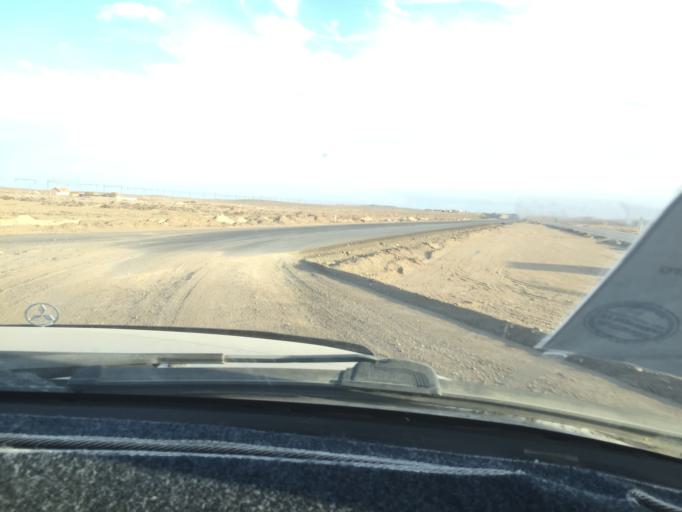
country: KZ
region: Almaty Oblysy
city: Ulken
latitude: 45.2401
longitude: 73.8284
